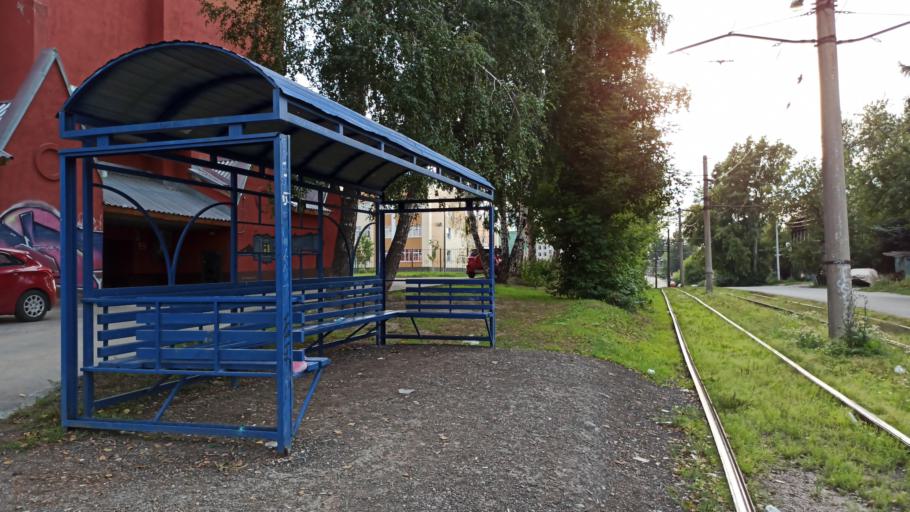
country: RU
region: Tomsk
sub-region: Tomskiy Rayon
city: Tomsk
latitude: 56.4795
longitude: 84.9619
